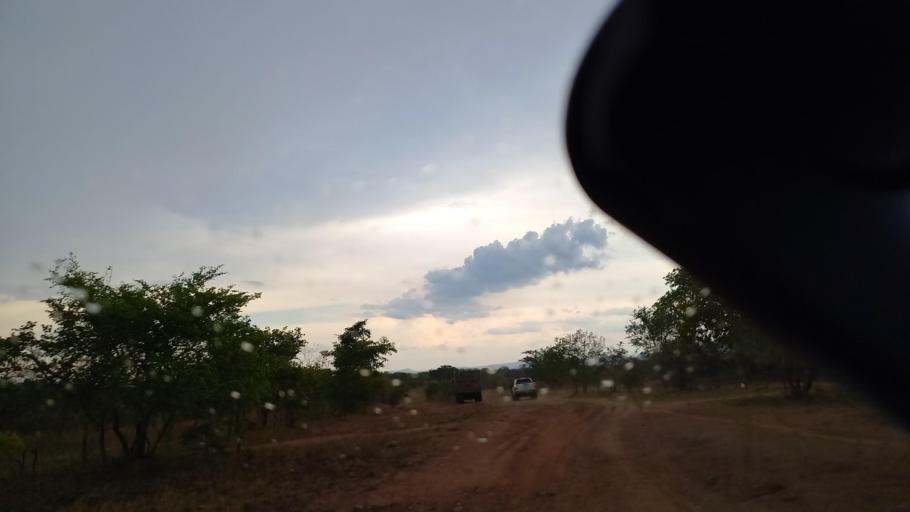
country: ZM
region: Lusaka
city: Kafue
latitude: -15.9805
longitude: 28.2582
